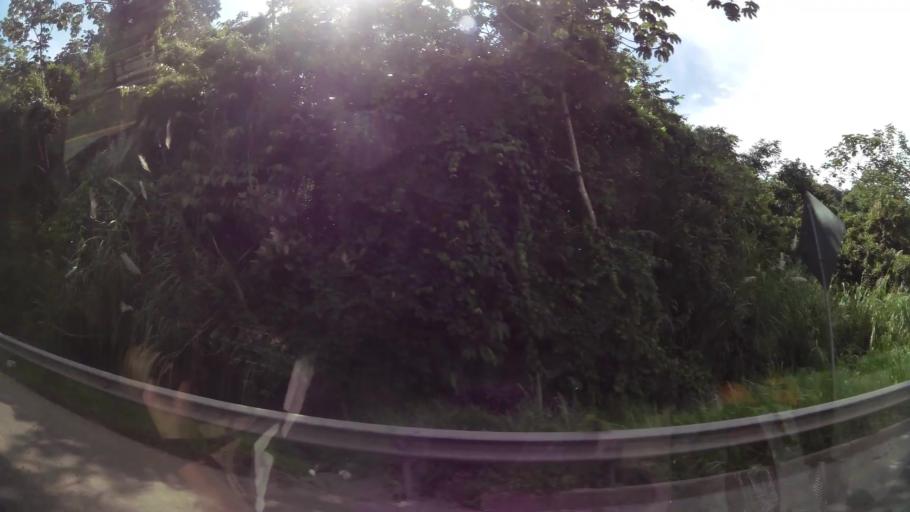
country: PA
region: Panama
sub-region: Distrito de Panama
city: Paraiso
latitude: 9.0316
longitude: -79.6151
